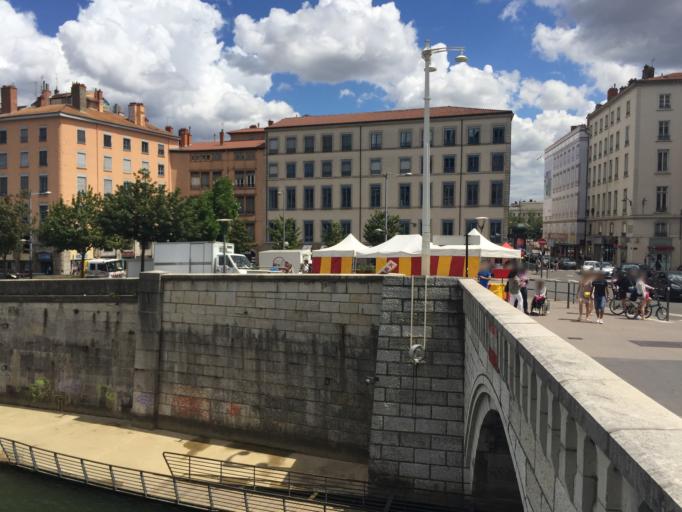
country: FR
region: Rhone-Alpes
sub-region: Departement du Rhone
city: Lyon
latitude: 45.7595
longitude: 4.8292
